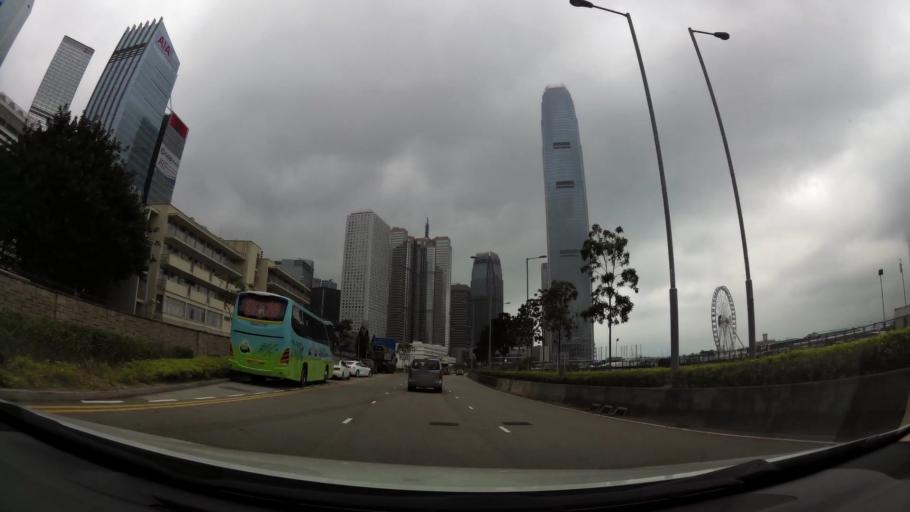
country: HK
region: Central and Western
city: Central
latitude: 22.2826
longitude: 114.1639
